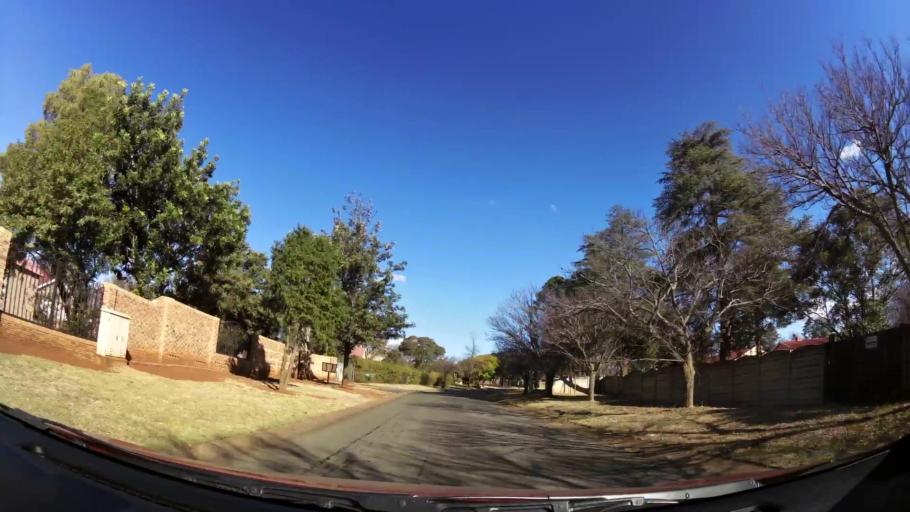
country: ZA
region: Gauteng
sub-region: West Rand District Municipality
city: Carletonville
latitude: -26.3712
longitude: 27.4095
